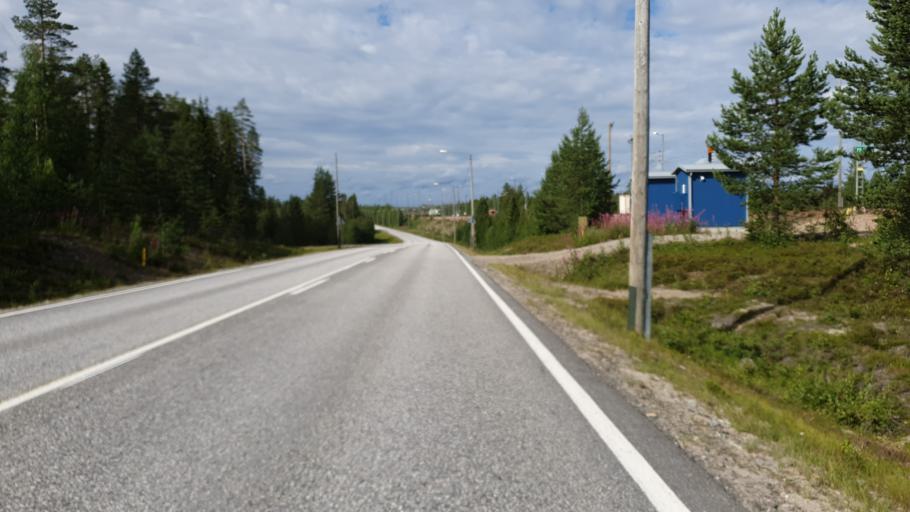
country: RU
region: Republic of Karelia
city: Kostomuksha
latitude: 64.5440
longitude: 29.9742
